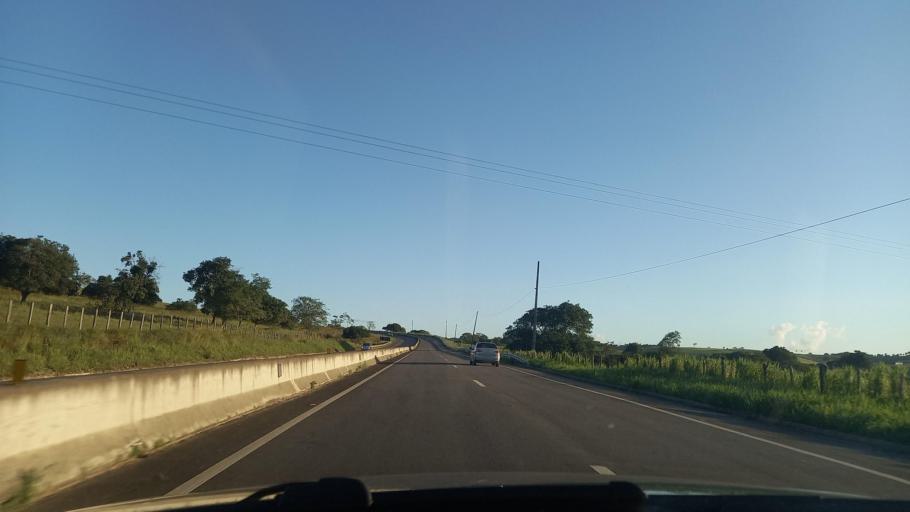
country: BR
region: Alagoas
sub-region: Limoeiro De Anadia
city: Limoeiro de Anadia
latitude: -9.7469
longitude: -36.5020
